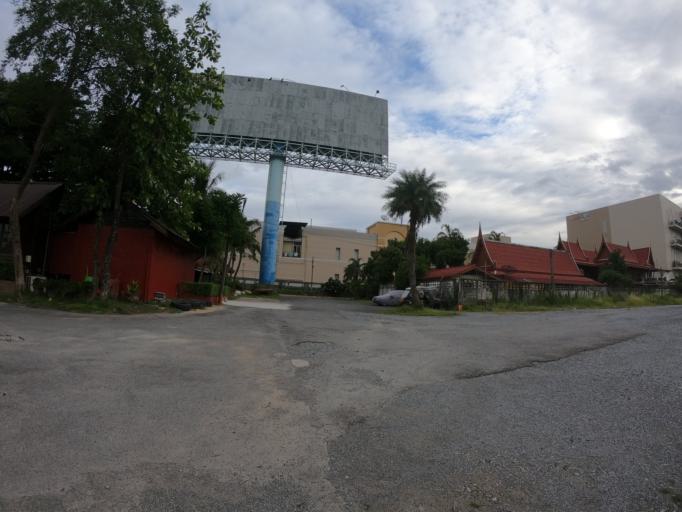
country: TH
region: Bangkok
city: Lat Phrao
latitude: 13.8296
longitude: 100.6281
